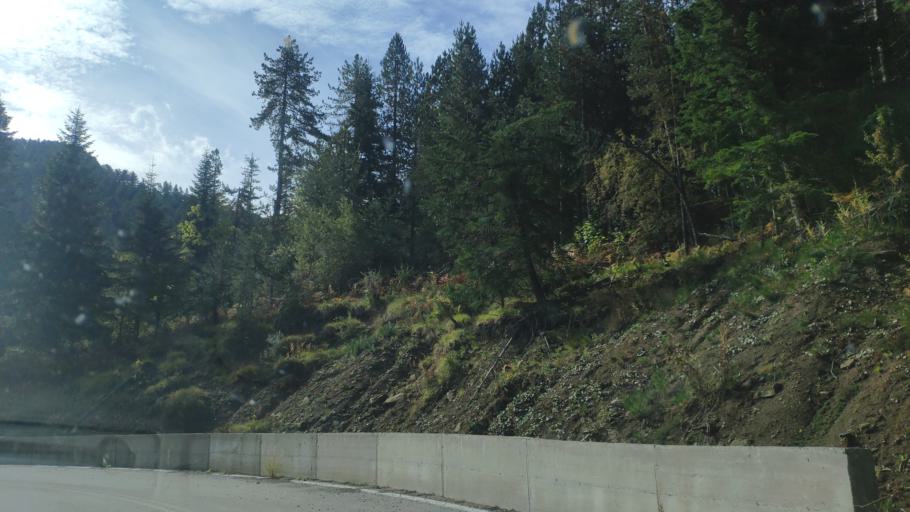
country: AL
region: Korce
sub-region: Rrethi i Devollit
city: Miras
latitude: 40.3999
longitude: 20.8953
